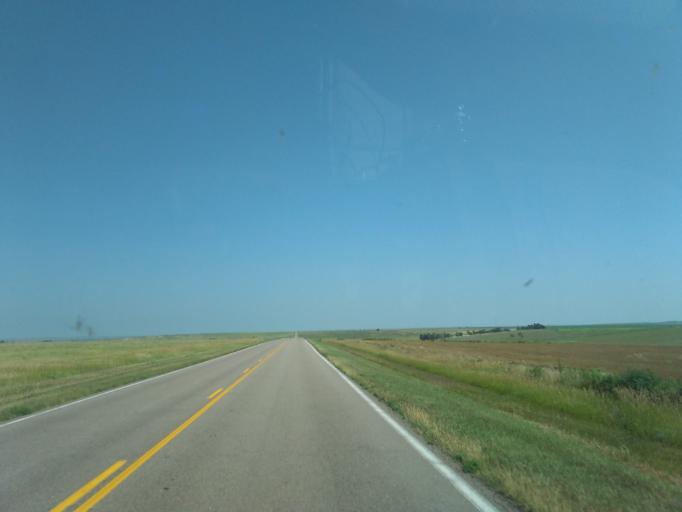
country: US
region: Nebraska
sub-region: Dundy County
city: Benkelman
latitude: 39.9249
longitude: -101.5413
